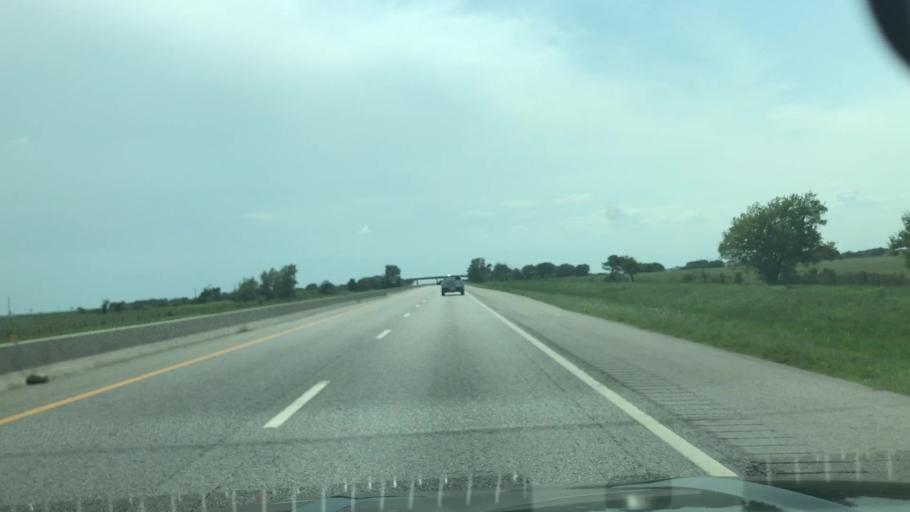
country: US
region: Oklahoma
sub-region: Ottawa County
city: Afton
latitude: 36.7023
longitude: -94.9907
